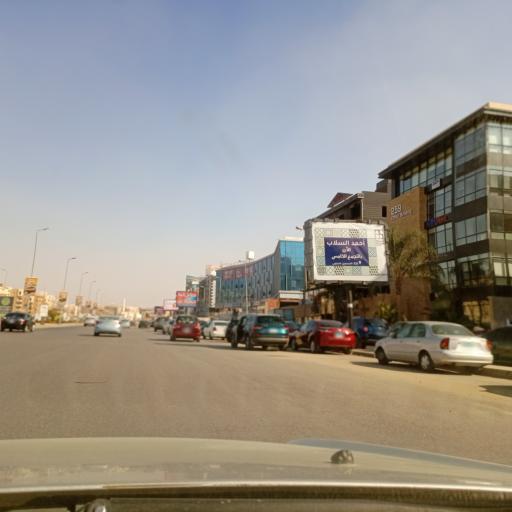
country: EG
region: Muhafazat al Qalyubiyah
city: Al Khankah
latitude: 30.0296
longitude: 31.4577
